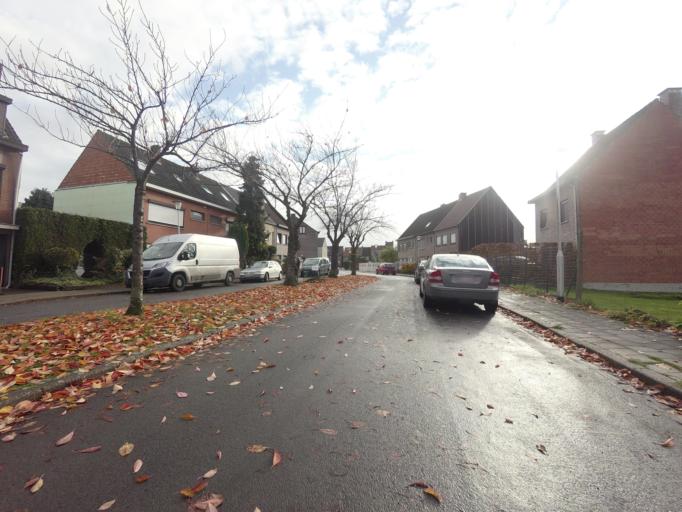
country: BE
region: Flanders
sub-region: Provincie Antwerpen
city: Niel
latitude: 51.1074
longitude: 4.3232
